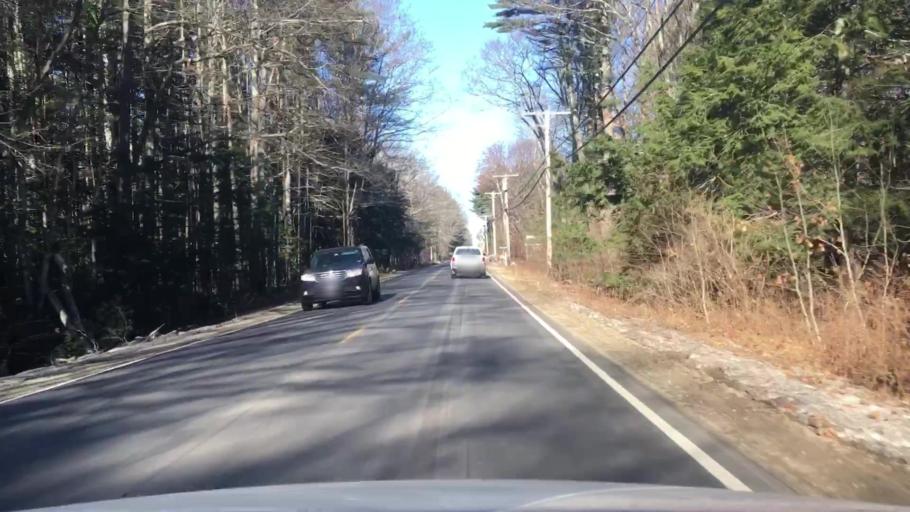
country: US
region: Maine
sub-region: York County
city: Arundel
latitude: 43.3914
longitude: -70.4821
